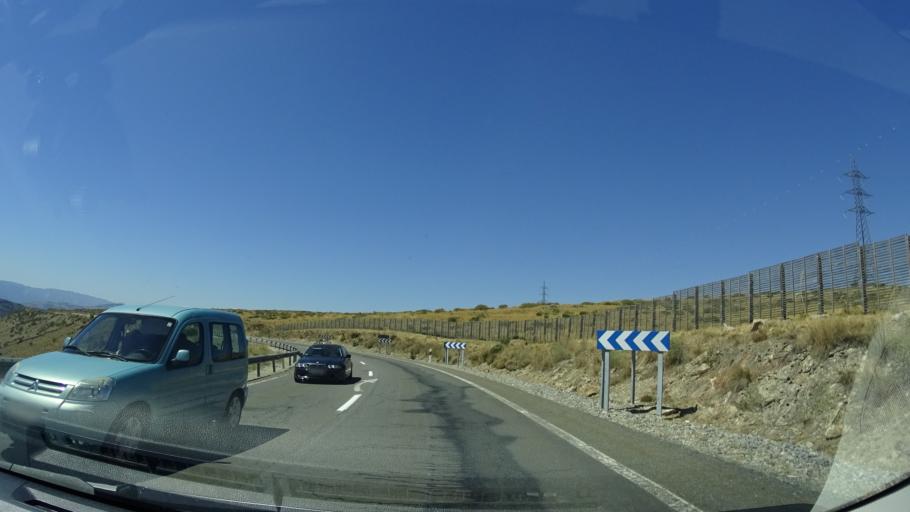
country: ES
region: Castille and Leon
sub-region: Provincia de Avila
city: Ojos-Albos
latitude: 40.6212
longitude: -4.5139
